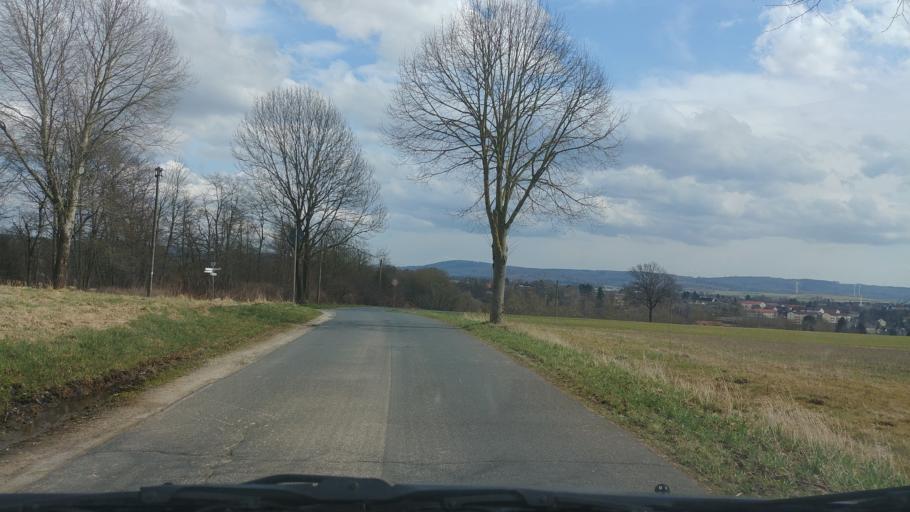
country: DE
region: Lower Saxony
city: Uslar
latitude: 51.6707
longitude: 9.6198
